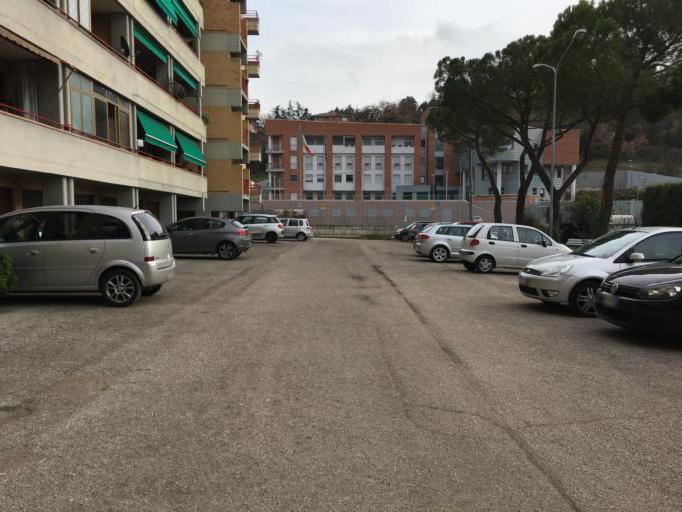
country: IT
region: Umbria
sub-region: Provincia di Perugia
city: Perugia
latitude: 43.0997
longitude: 12.3731
